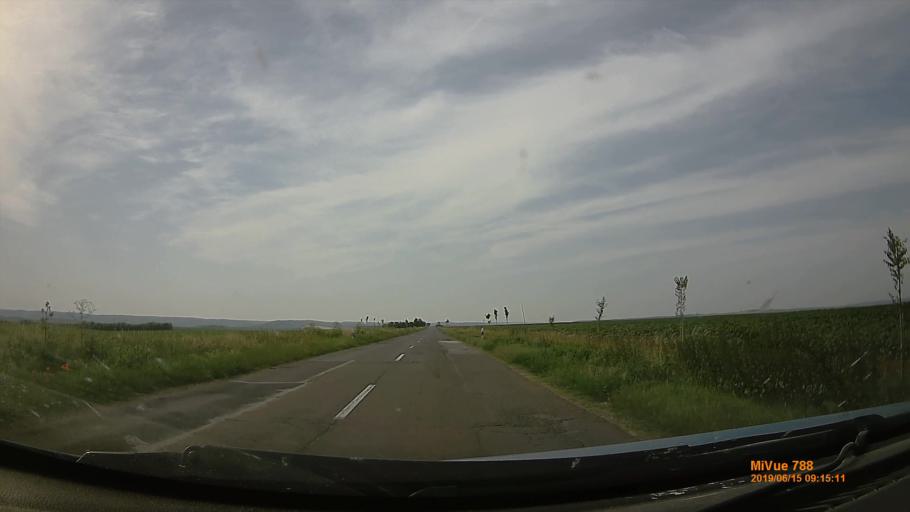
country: HU
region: Tolna
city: Iregszemcse
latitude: 46.6332
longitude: 18.1994
